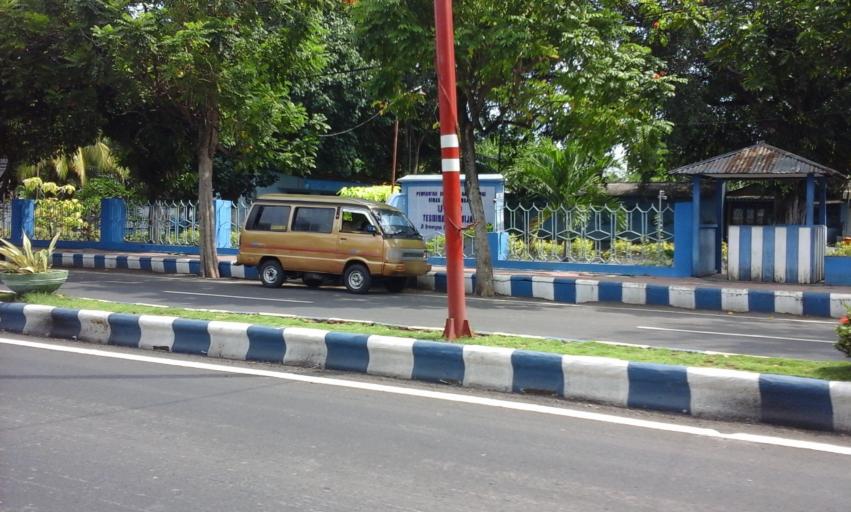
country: ID
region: East Java
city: Banyuwangi
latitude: -8.2342
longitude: 114.3557
